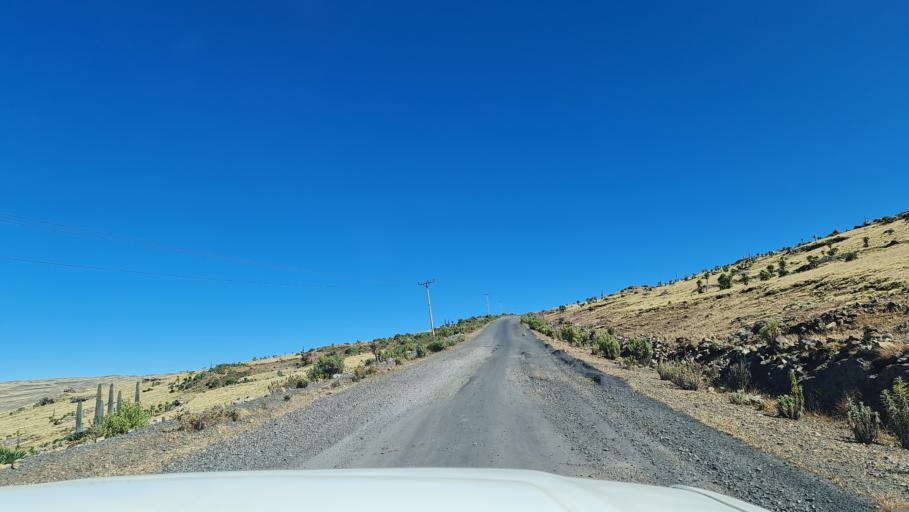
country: ET
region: Amhara
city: Debark'
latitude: 13.1648
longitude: 38.1949
